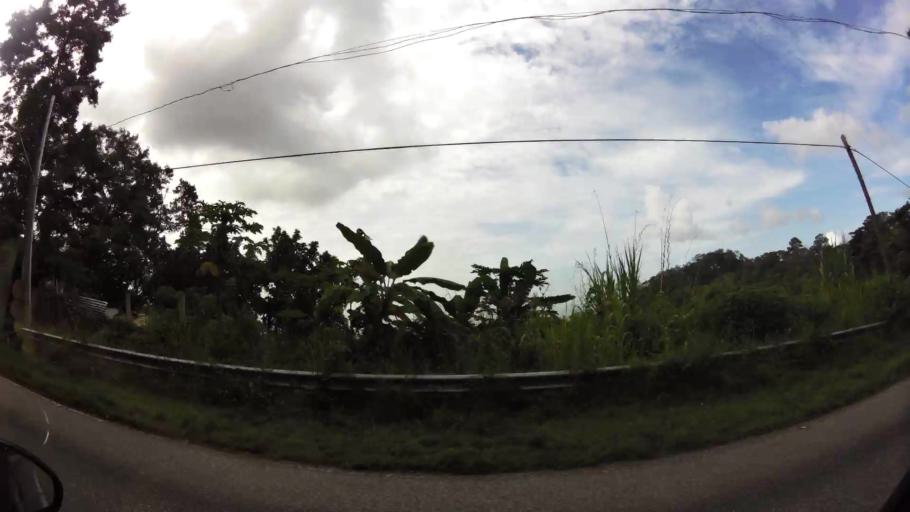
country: TT
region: City of Port of Spain
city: Port-of-Spain
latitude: 10.6758
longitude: -61.4935
